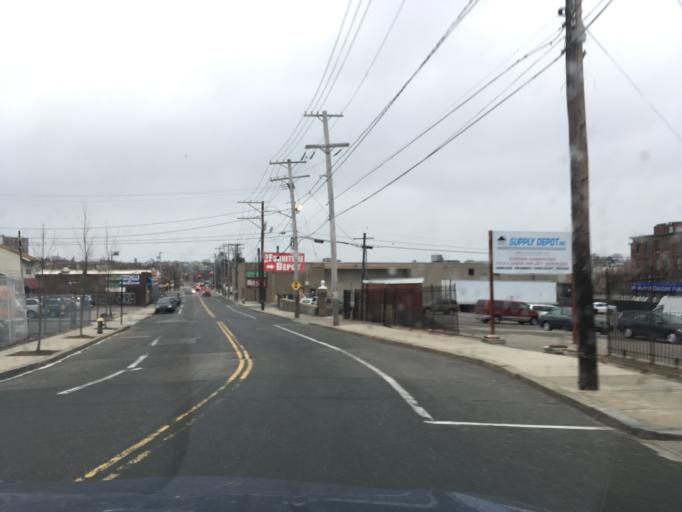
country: US
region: Rhode Island
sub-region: Providence County
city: Providence
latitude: 41.8191
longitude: -71.4461
